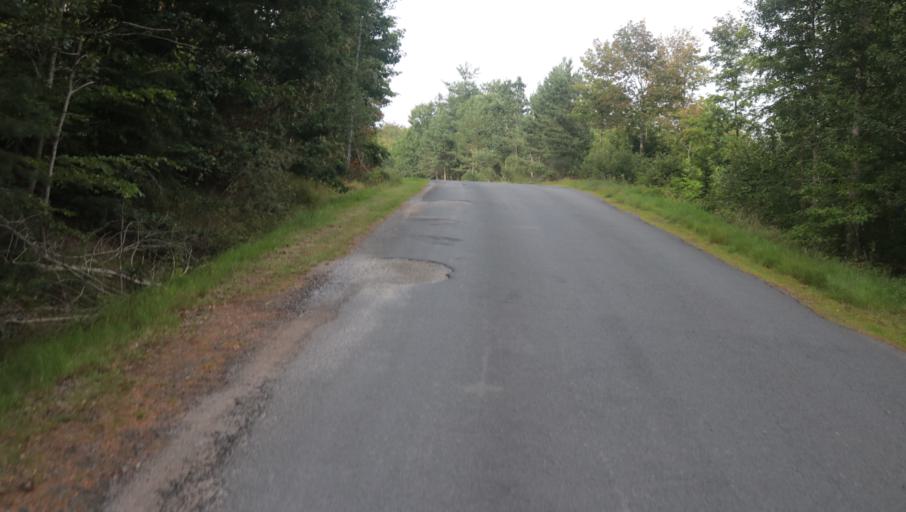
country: SE
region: Blekinge
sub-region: Karlshamns Kommun
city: Karlshamn
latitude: 56.2077
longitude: 14.8745
